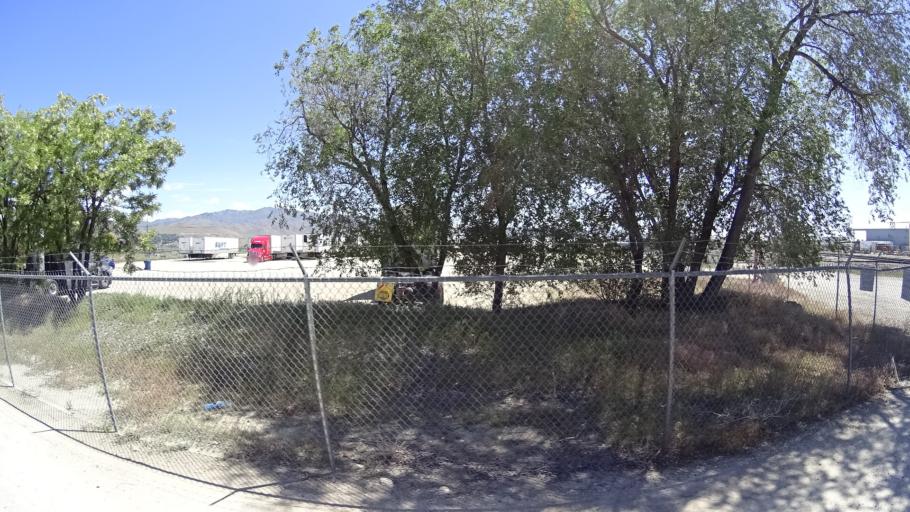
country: US
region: Idaho
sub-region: Ada County
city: Boise
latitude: 43.5637
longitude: -116.1834
